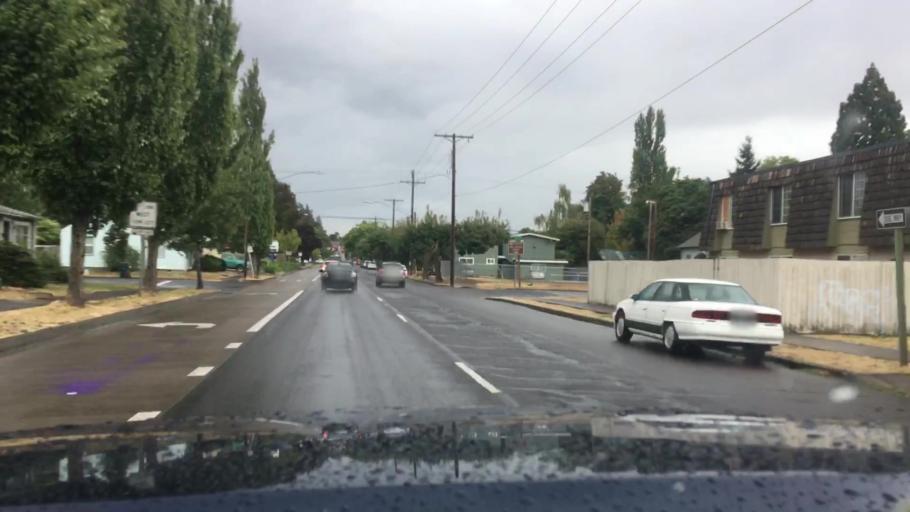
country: US
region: Oregon
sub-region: Lane County
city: Springfield
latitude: 44.0493
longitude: -123.0233
